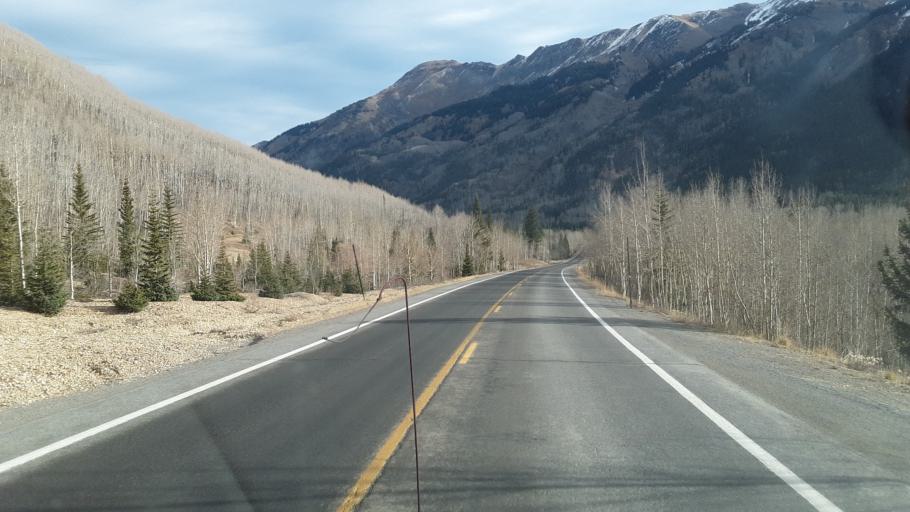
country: US
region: Colorado
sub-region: Ouray County
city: Ouray
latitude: 37.9363
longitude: -107.6790
